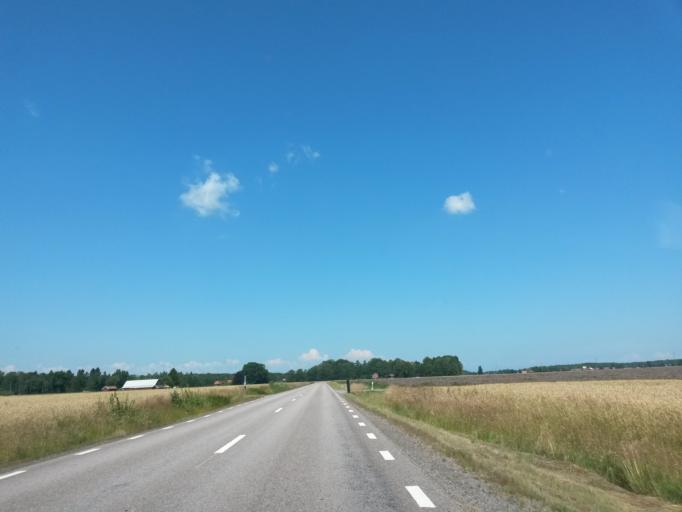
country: SE
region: Vaestra Goetaland
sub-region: Grastorps Kommun
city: Graestorp
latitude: 58.2875
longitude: 12.6709
